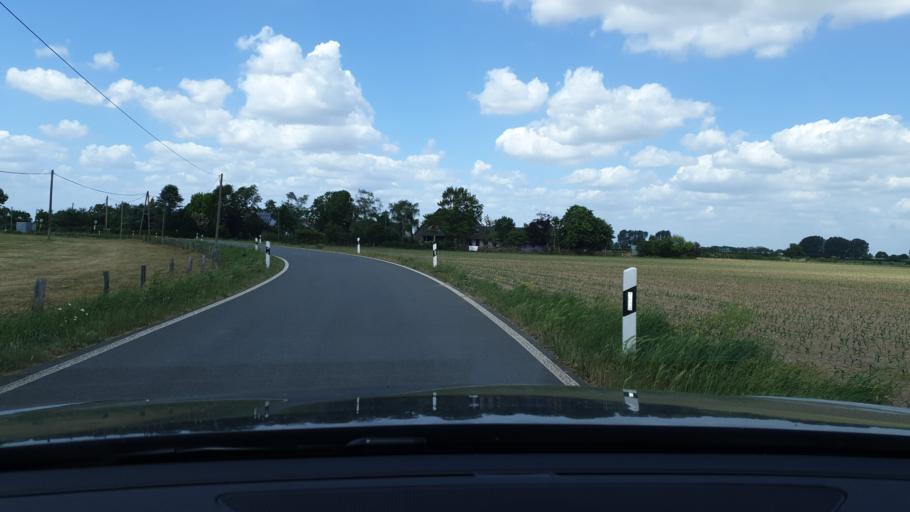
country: DE
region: North Rhine-Westphalia
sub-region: Regierungsbezirk Dusseldorf
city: Kranenburg
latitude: 51.8184
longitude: 6.0473
